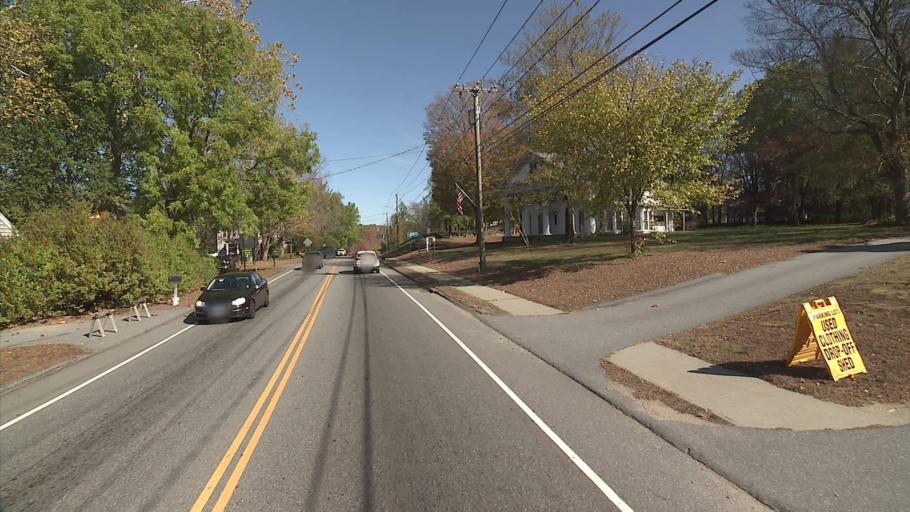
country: US
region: Connecticut
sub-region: Windham County
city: East Brooklyn
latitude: 41.7887
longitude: -71.9492
